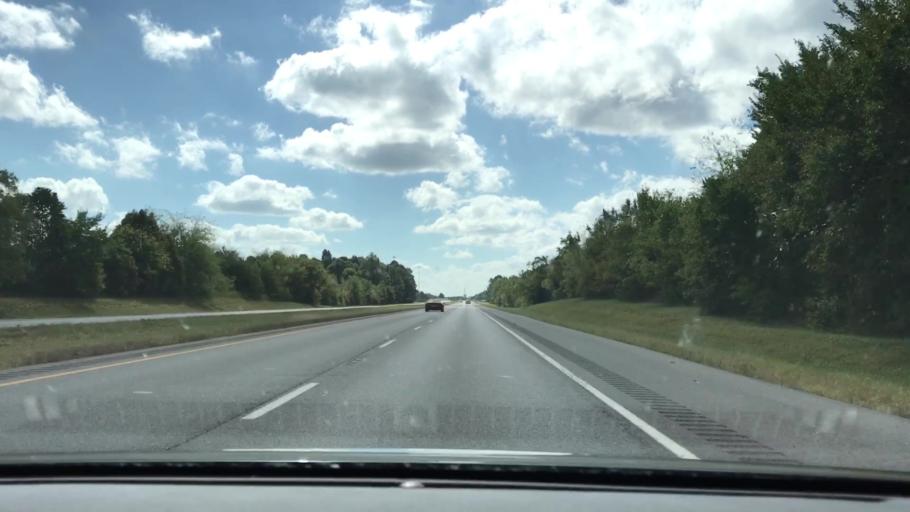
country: US
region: Kentucky
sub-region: McCracken County
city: Reidland
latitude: 37.0015
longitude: -88.5068
